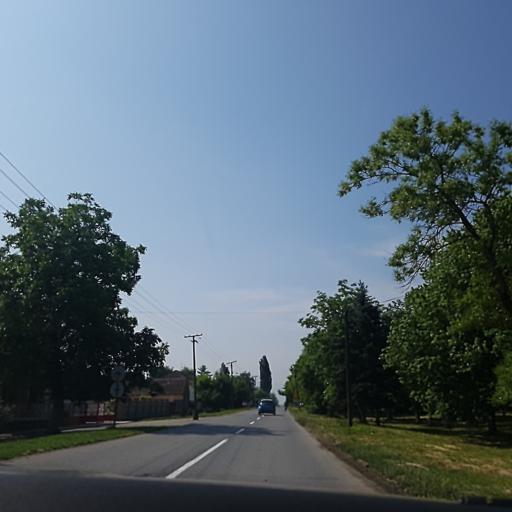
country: RS
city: Jarkovac
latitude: 45.2715
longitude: 20.7645
